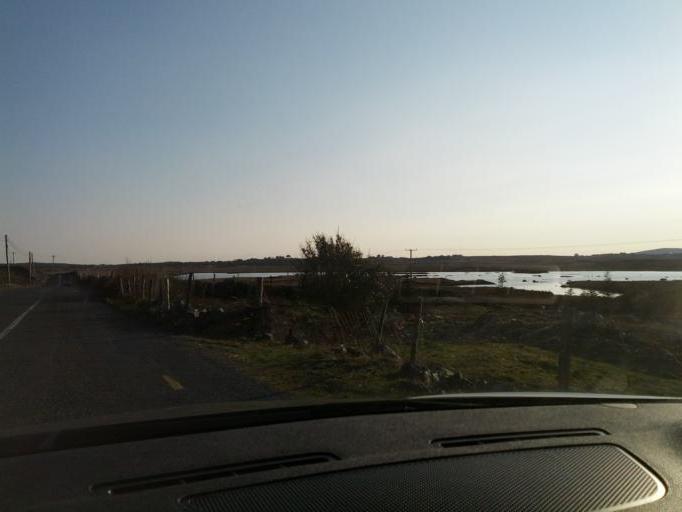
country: IE
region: Connaught
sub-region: County Galway
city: Oughterard
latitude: 53.3180
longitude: -9.5505
